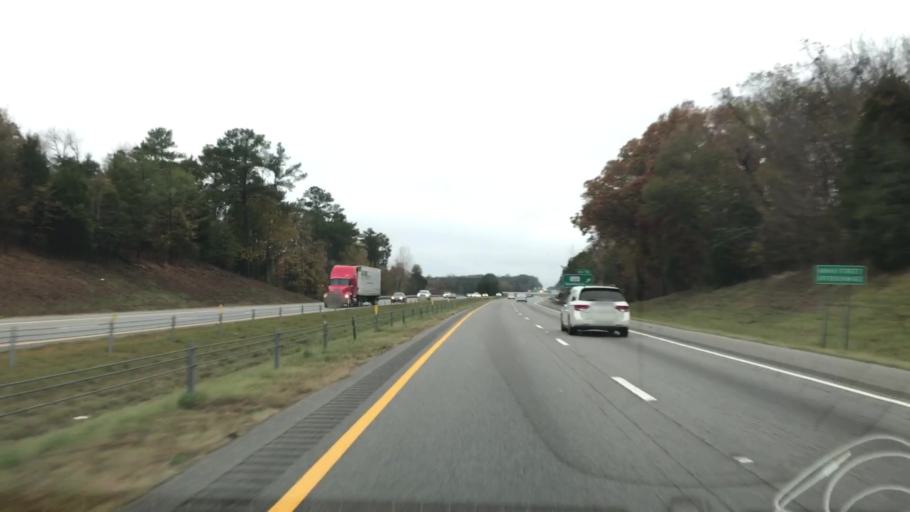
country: US
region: South Carolina
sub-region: Newberry County
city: Prosperity
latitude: 34.2890
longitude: -81.5394
